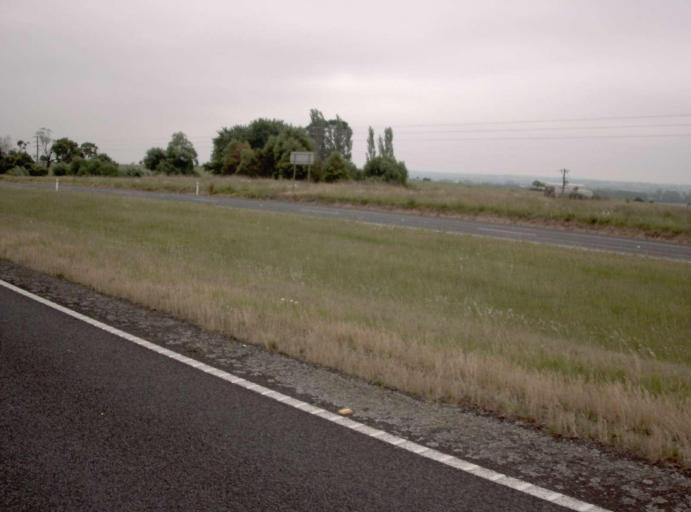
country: AU
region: Victoria
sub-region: Latrobe
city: Moe
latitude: -38.1928
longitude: 146.2113
